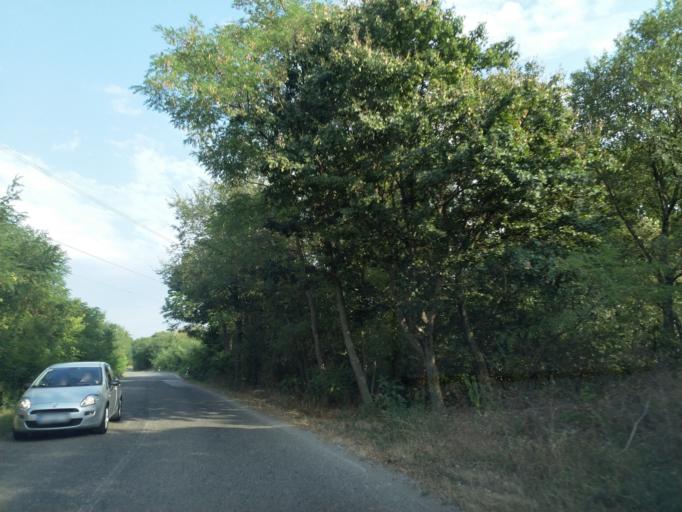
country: RS
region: Central Serbia
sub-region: Pomoravski Okrug
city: Paracin
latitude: 43.8503
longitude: 21.4471
